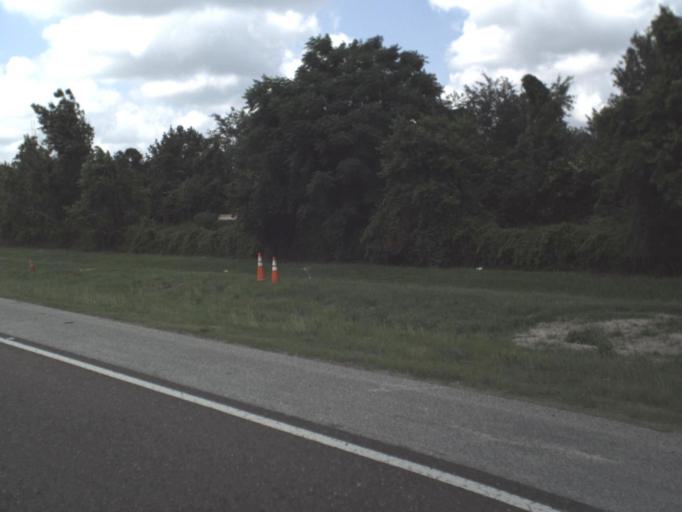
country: US
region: Florida
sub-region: Saint Johns County
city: Fruit Cove
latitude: 30.1534
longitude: -81.5478
